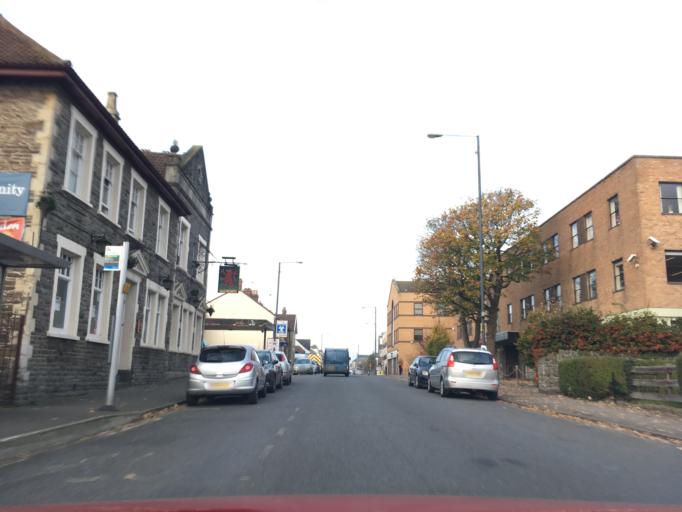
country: GB
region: England
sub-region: South Gloucestershire
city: Mangotsfield
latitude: 51.4809
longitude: -2.5016
